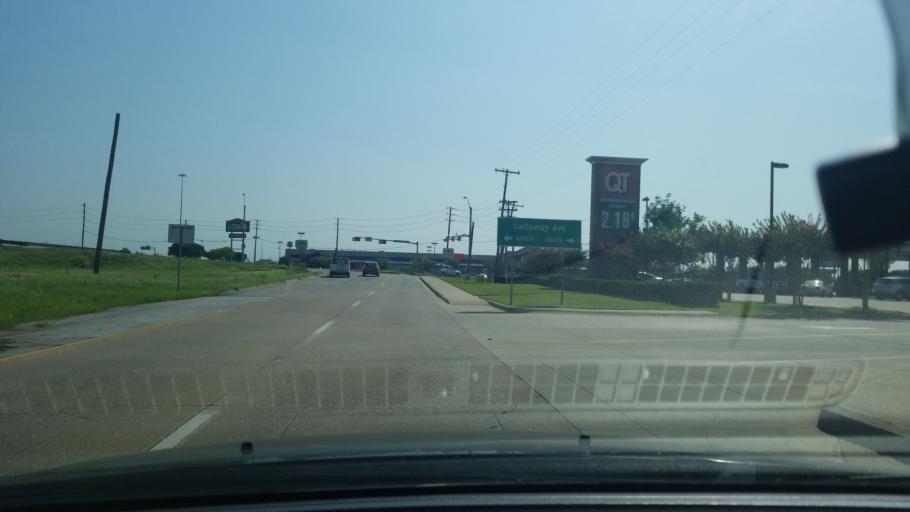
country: US
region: Texas
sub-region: Dallas County
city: Mesquite
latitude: 32.8244
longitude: -96.6247
